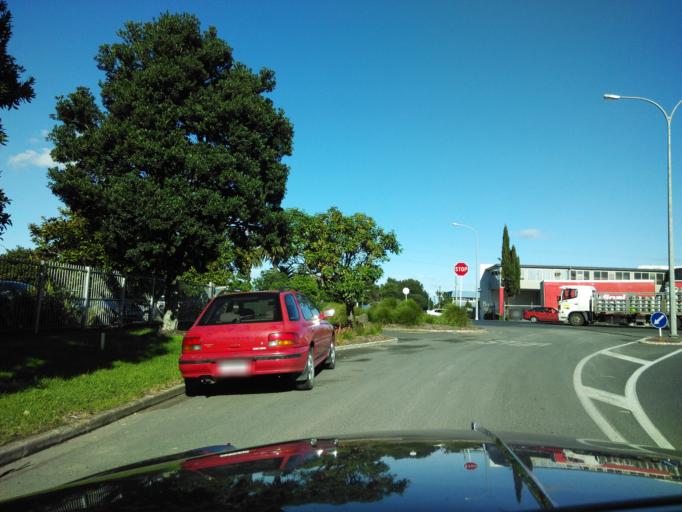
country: NZ
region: Auckland
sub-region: Auckland
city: Mangere
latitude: -36.9260
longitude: 174.7949
